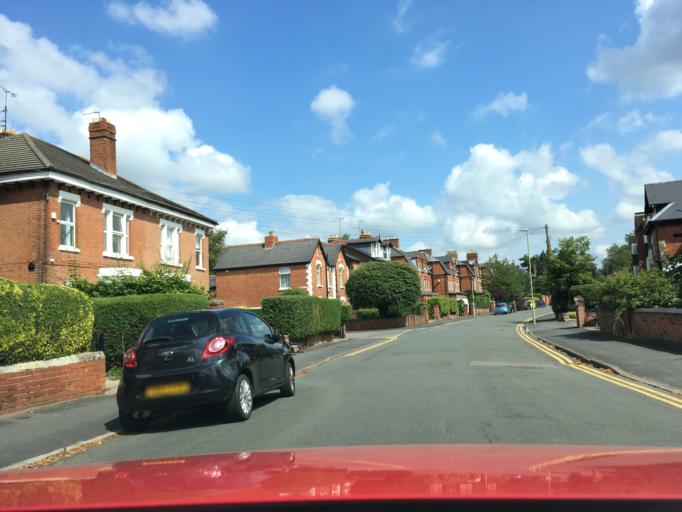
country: GB
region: England
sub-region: Gloucestershire
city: Gloucester
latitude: 51.8696
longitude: -2.2347
